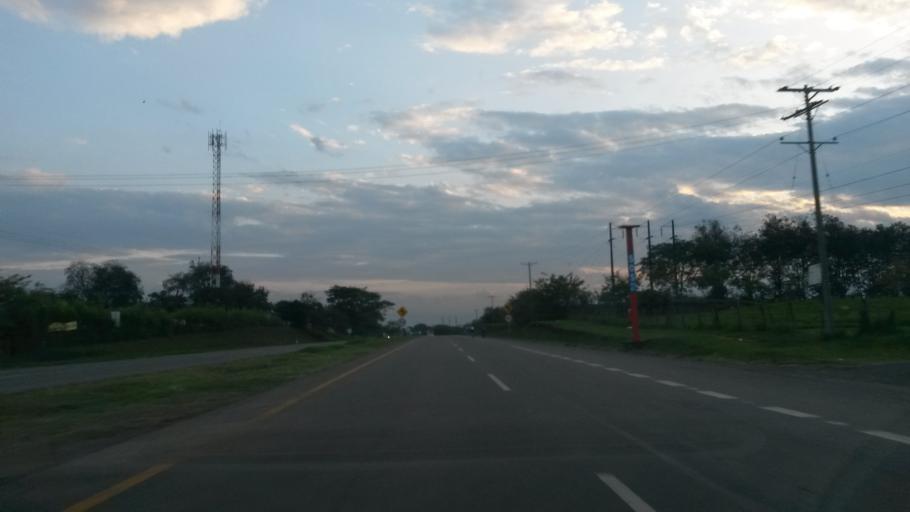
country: CO
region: Cauca
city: Santander de Quilichao
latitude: 3.0854
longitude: -76.4725
